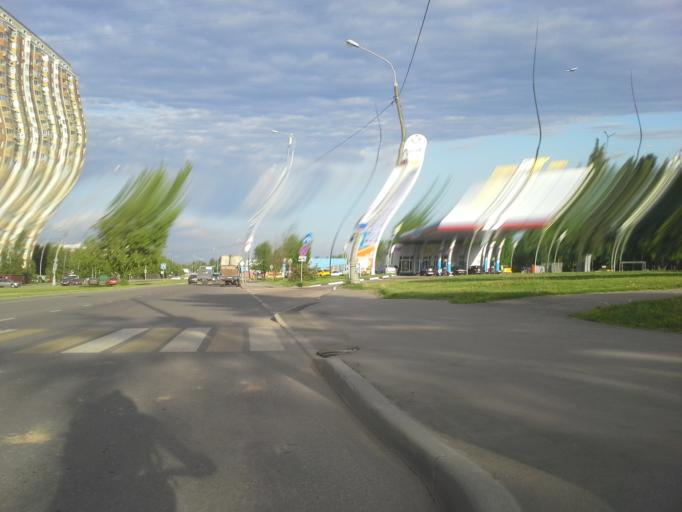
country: RU
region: Moscow
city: Solntsevo
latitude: 55.6419
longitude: 37.4065
